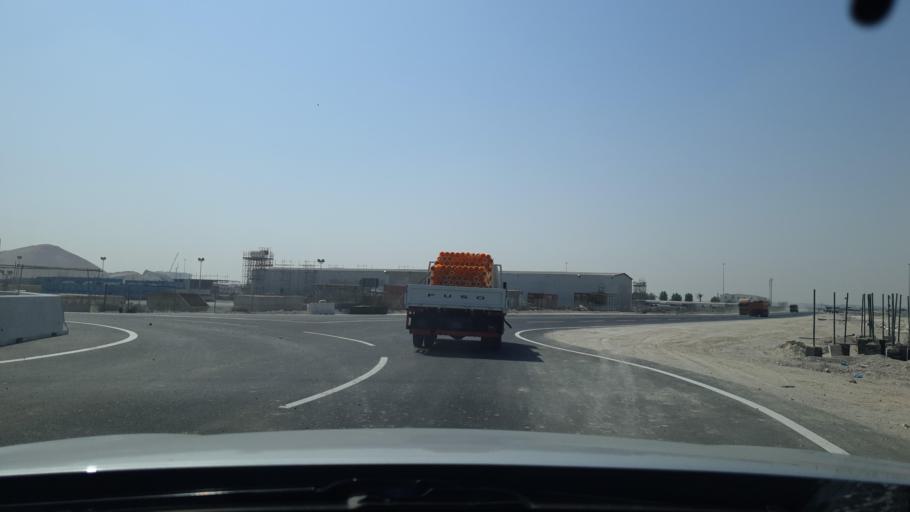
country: QA
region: Baladiyat ad Dawhah
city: Doha
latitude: 25.2251
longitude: 51.5205
